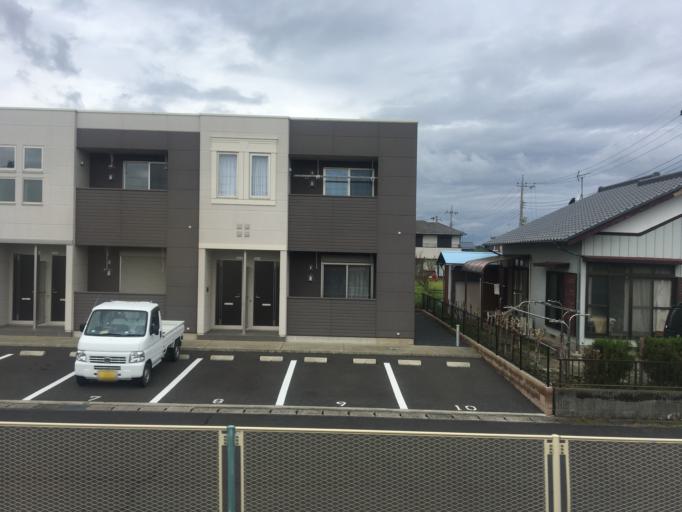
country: JP
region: Chiba
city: Togane
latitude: 35.5451
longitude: 140.3406
